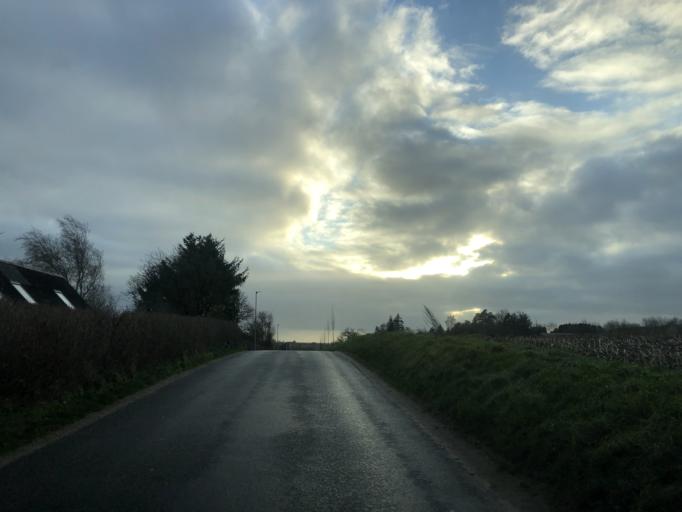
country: DK
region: Central Jutland
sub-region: Viborg Kommune
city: Viborg
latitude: 56.4790
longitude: 9.3424
